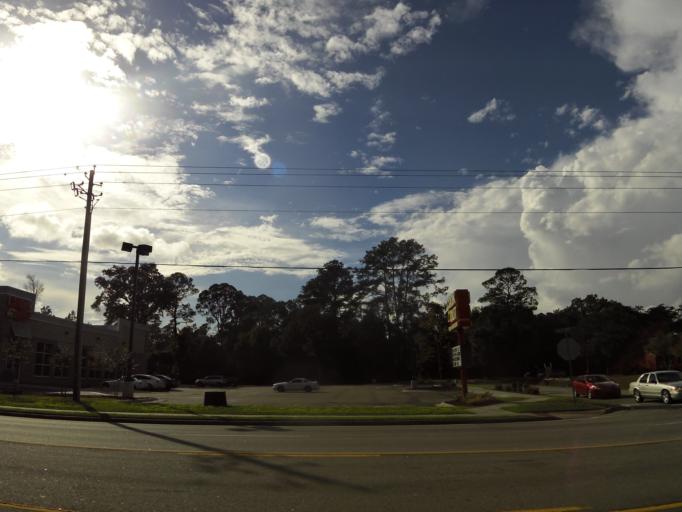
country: US
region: Georgia
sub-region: Liberty County
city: Hinesville
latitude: 31.8300
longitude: -81.5975
